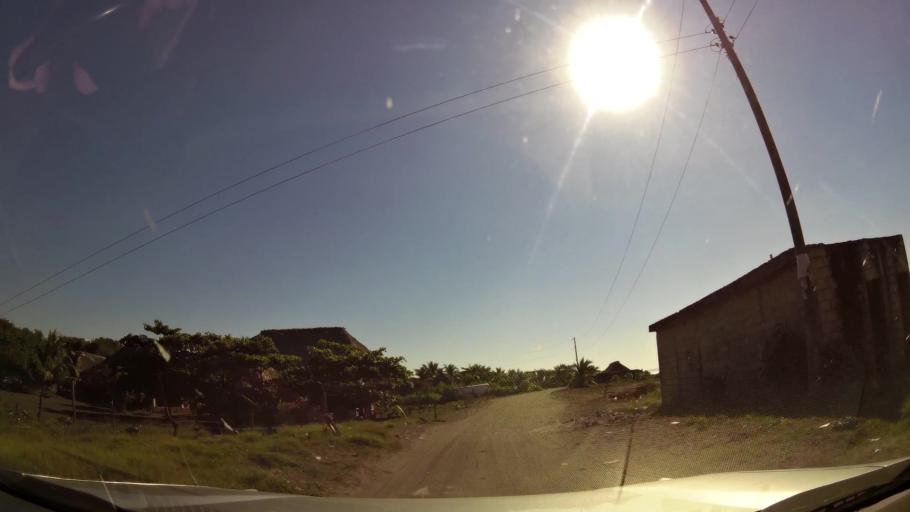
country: GT
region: Jutiapa
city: Pasaco
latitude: 13.8477
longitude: -90.3699
